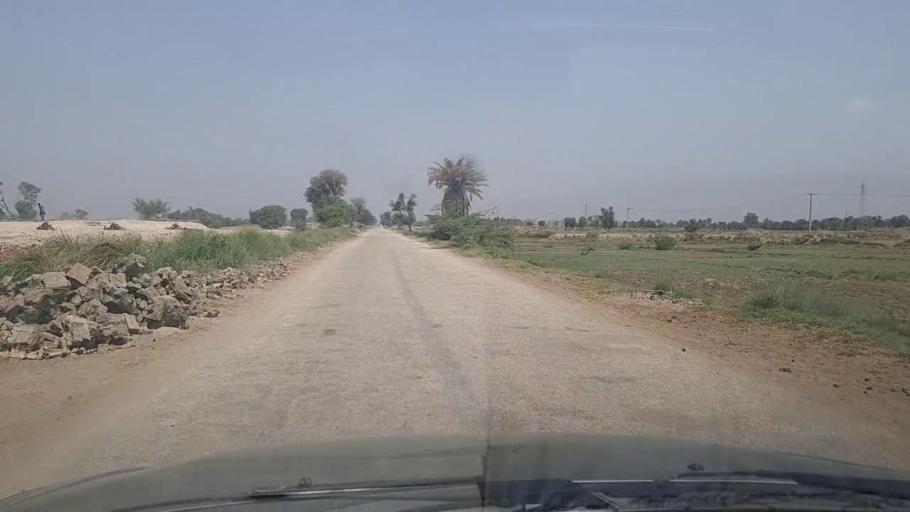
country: PK
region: Sindh
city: Setharja Old
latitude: 27.1451
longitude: 68.5257
